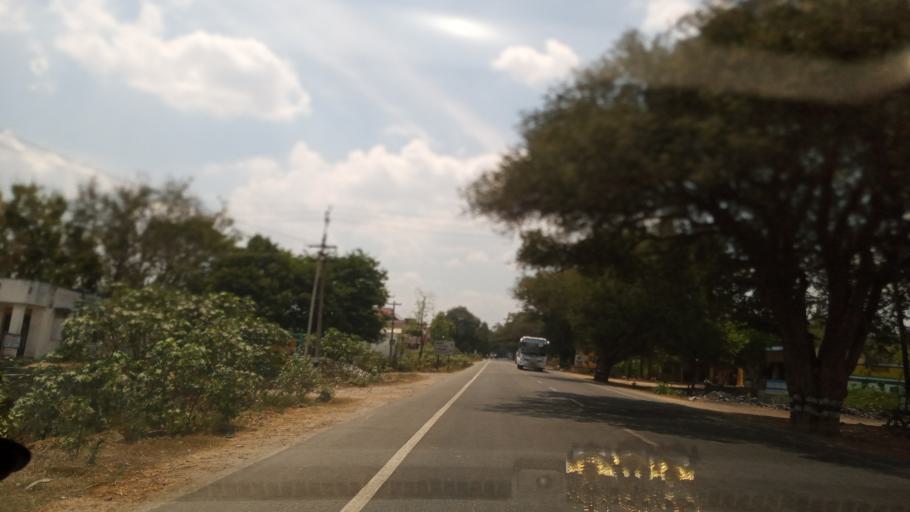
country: IN
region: Tamil Nadu
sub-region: Vellore
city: Walajapet
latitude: 12.9188
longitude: 79.3841
